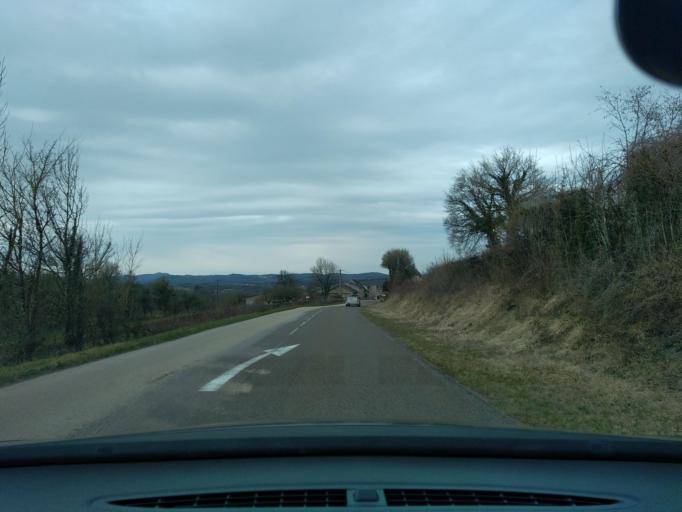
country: FR
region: Franche-Comte
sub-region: Departement du Jura
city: Orgelet
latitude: 46.4739
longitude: 5.5754
